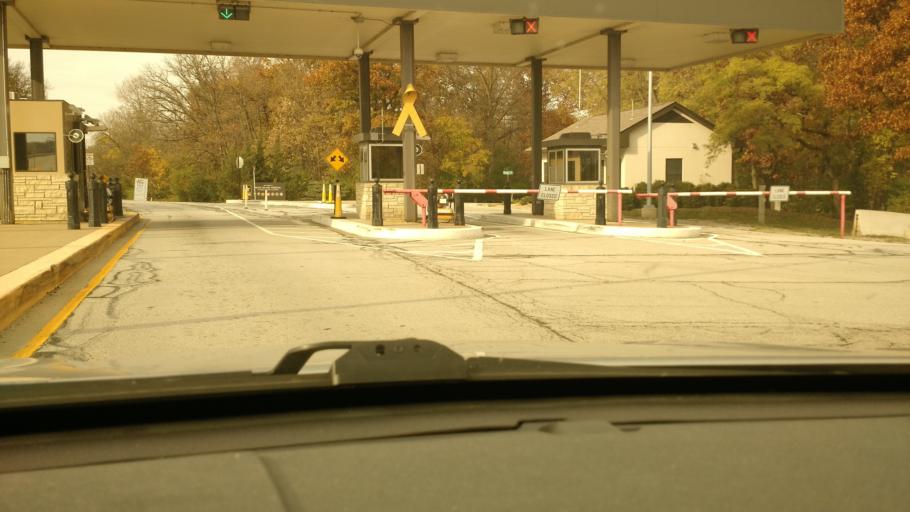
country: US
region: Illinois
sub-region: Rock Island County
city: Moline
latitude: 41.5131
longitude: -90.5208
